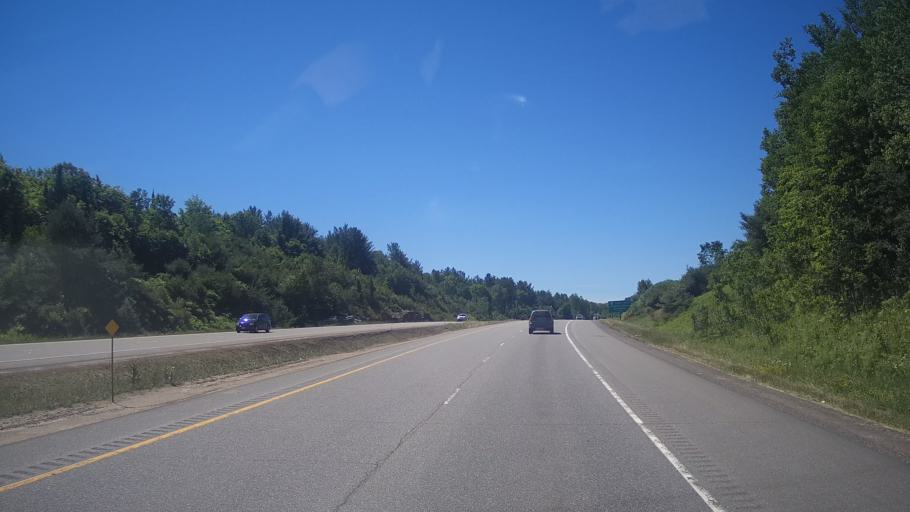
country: CA
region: Ontario
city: Bracebridge
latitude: 45.0265
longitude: -79.2923
